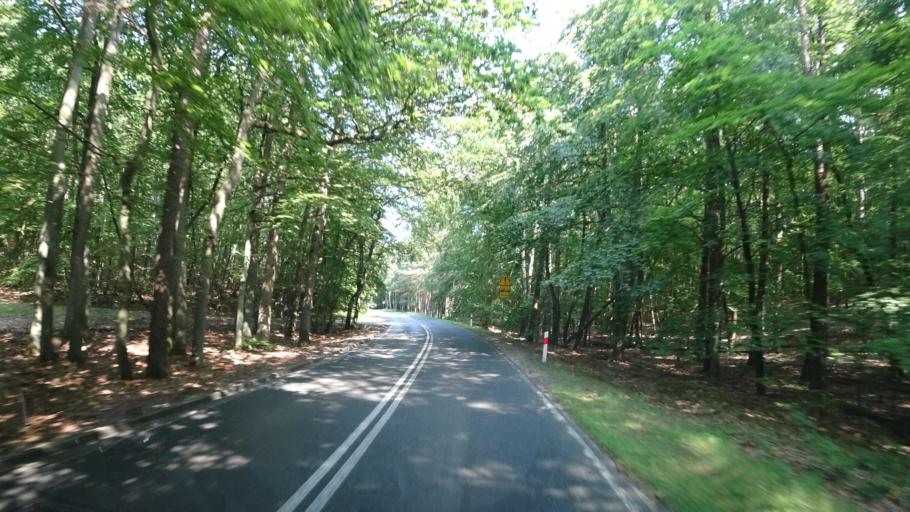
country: PL
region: West Pomeranian Voivodeship
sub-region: Powiat kamienski
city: Miedzyzdroje
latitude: 53.9631
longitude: 14.5385
